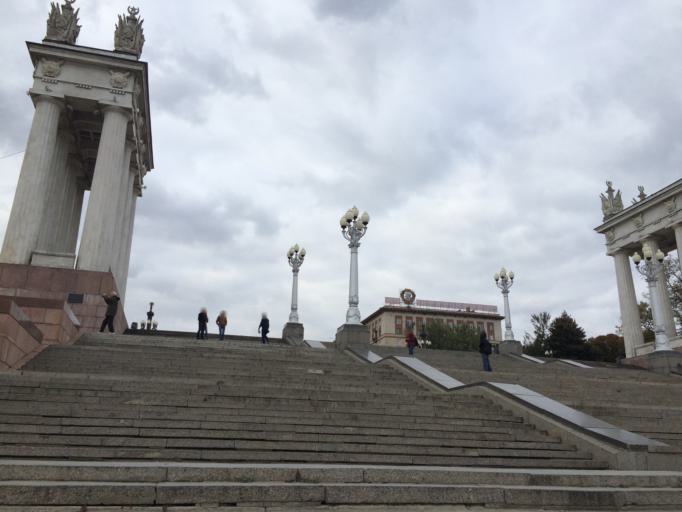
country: RU
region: Volgograd
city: Volgograd
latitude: 48.7038
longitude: 44.5214
